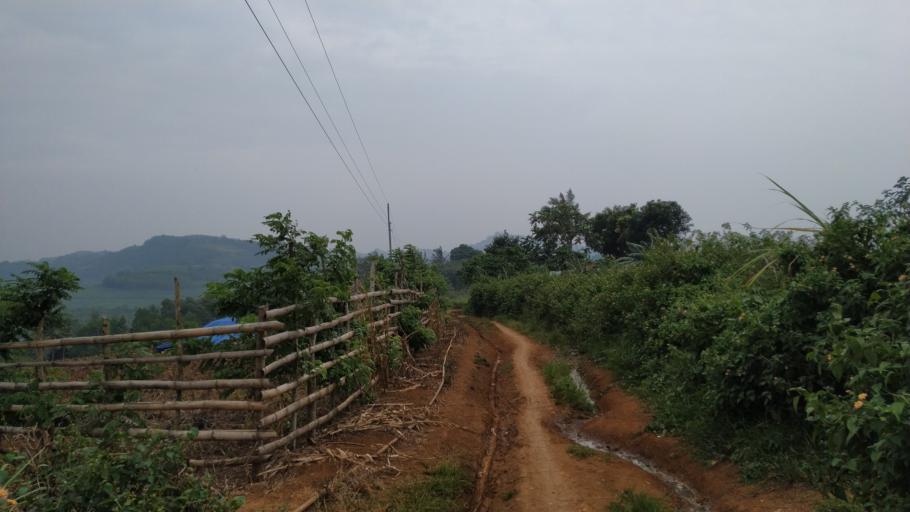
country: PH
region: Western Visayas
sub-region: Province of Negros Occidental
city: Quezon
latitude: 10.4219
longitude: 123.2401
